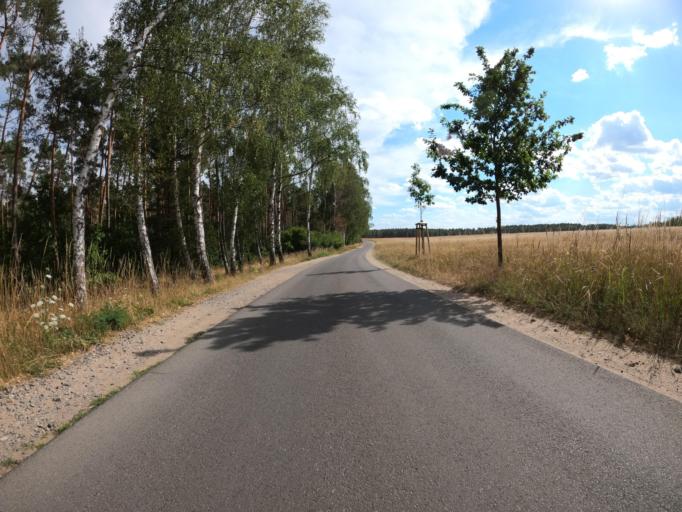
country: DE
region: Brandenburg
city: Lychen
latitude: 53.2955
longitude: 13.4286
